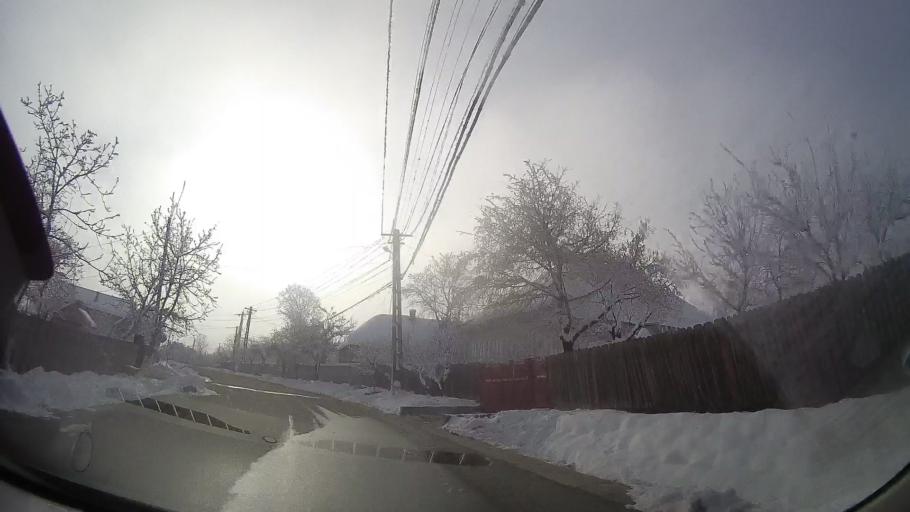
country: RO
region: Iasi
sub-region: Comuna Valea Seaca
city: Topile
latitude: 47.2516
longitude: 26.6616
